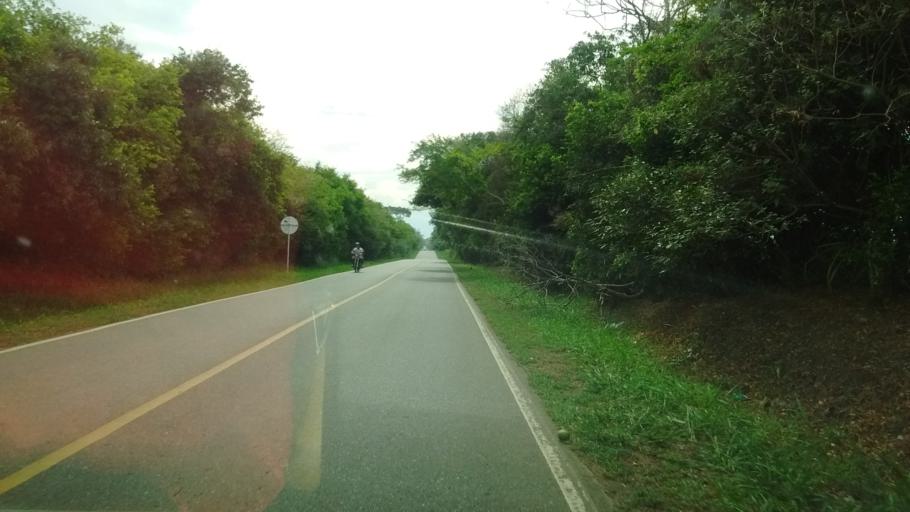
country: CO
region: Cauca
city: Caloto
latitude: 3.0469
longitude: -76.4336
